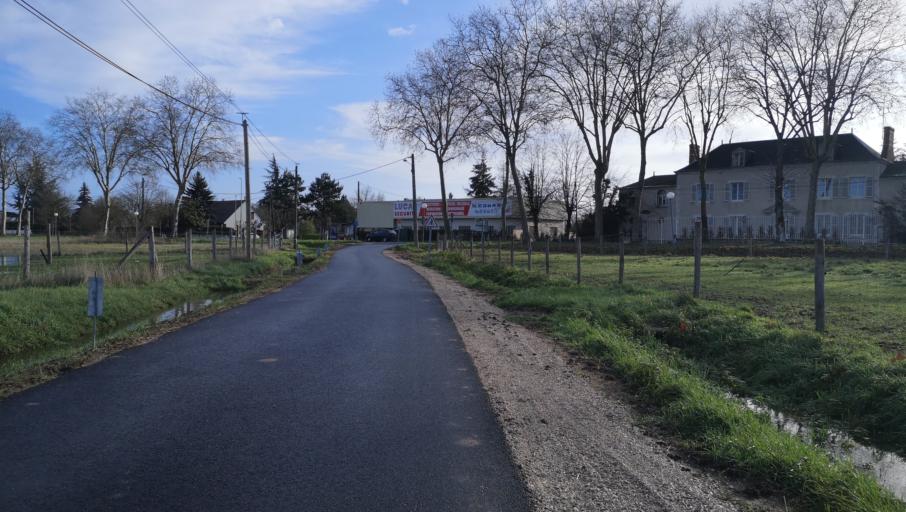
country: FR
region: Centre
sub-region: Departement du Loiret
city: Saint-Pryve-Saint-Mesmin
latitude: 47.8775
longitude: 1.8532
